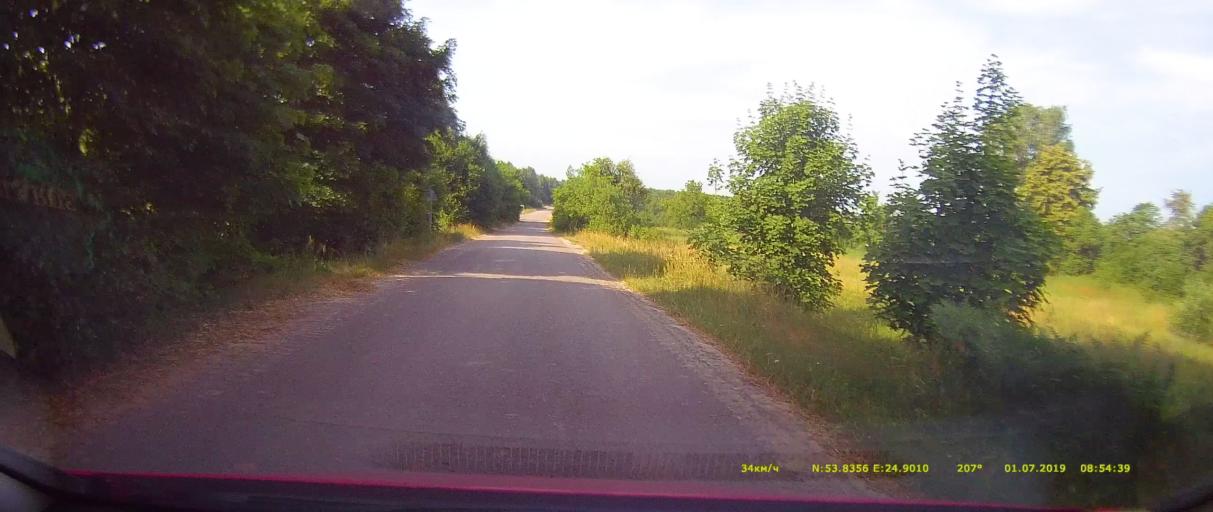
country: BY
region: Grodnenskaya
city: Shchuchin
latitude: 53.8358
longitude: 24.9011
